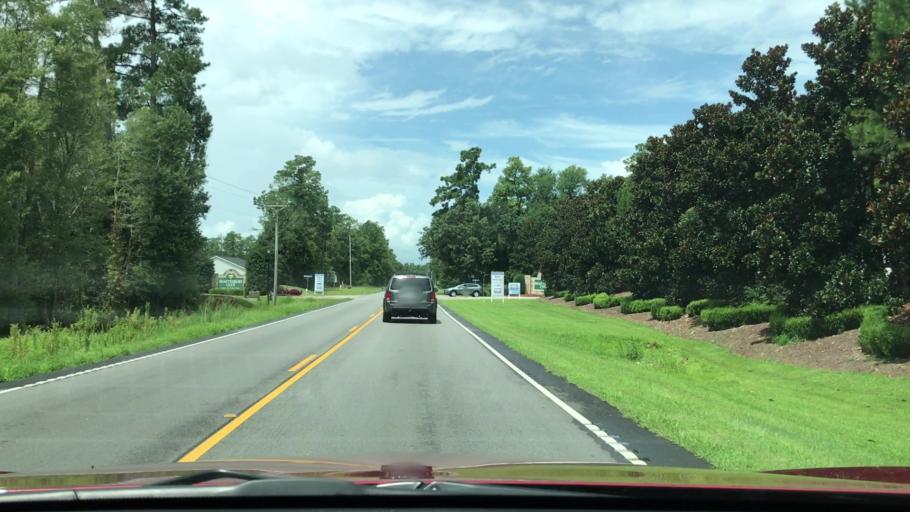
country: US
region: South Carolina
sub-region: Horry County
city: Red Hill
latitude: 33.9029
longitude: -78.9011
